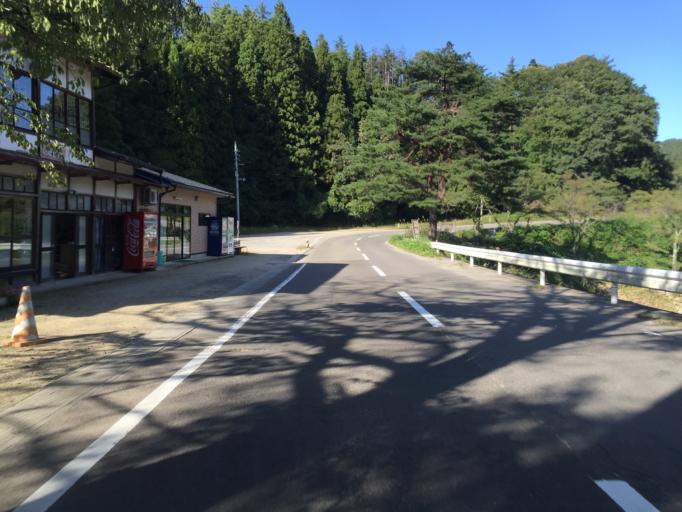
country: JP
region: Miyagi
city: Marumori
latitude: 37.8699
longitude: 140.7816
